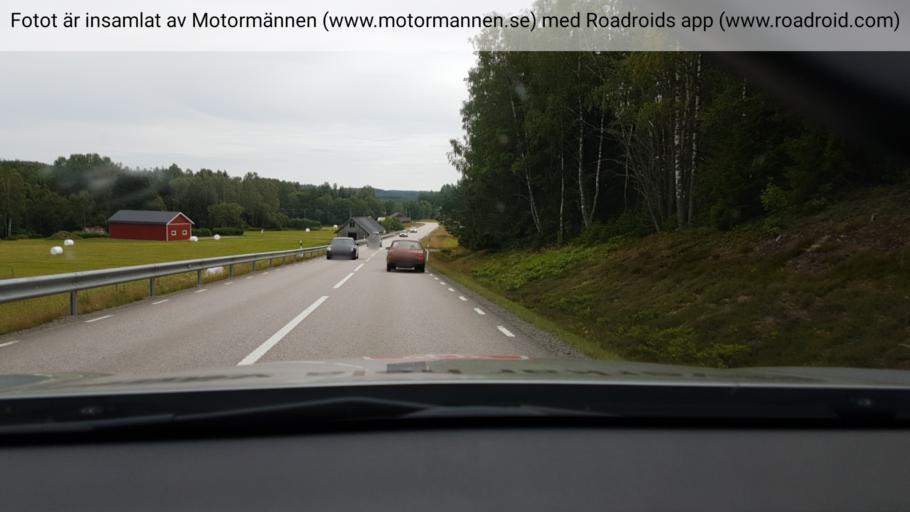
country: SE
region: Vaestra Goetaland
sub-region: Bengtsfors Kommun
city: Dals Langed
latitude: 58.8917
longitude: 12.2108
